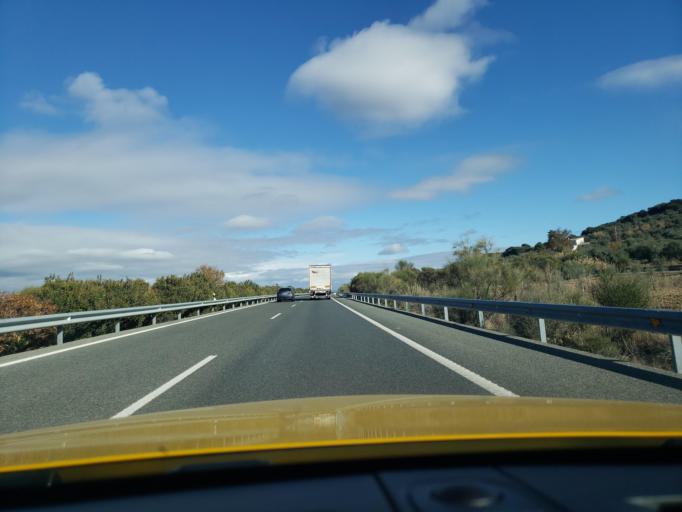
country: ES
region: Andalusia
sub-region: Provincia de Malaga
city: Villanueva de Tapia
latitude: 37.1074
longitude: -4.3101
